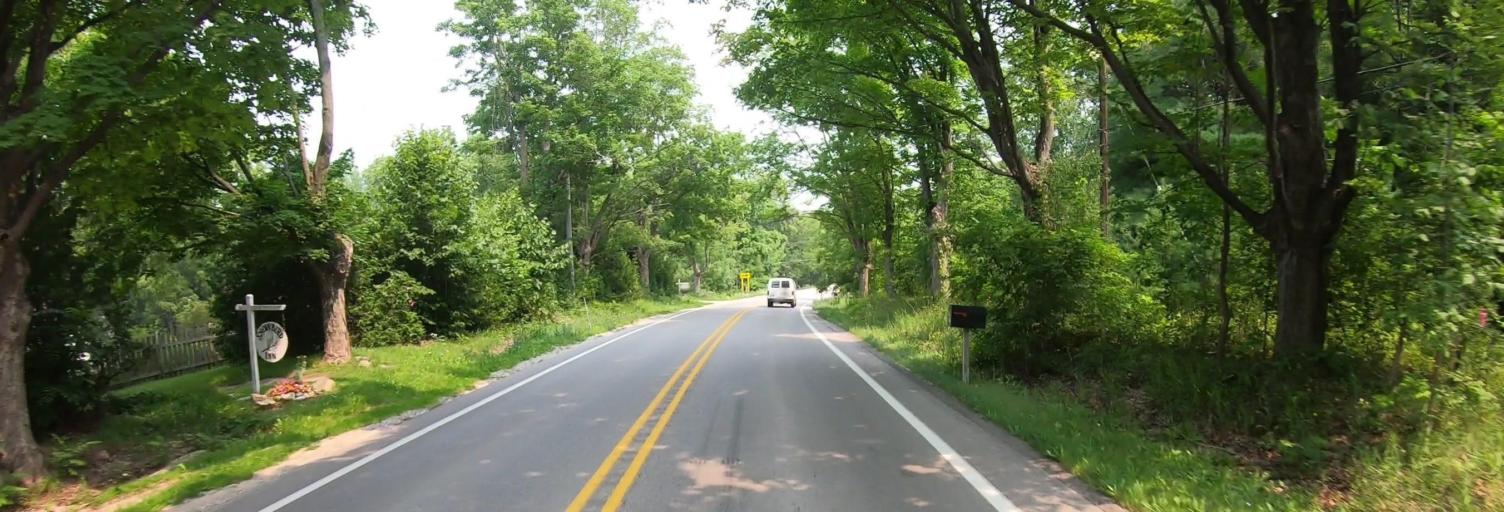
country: US
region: Michigan
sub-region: Leelanau County
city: Leland
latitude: 44.9884
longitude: -85.7725
